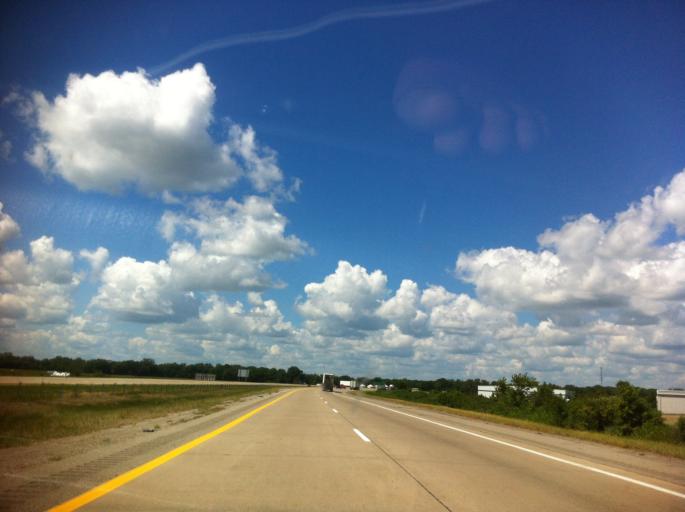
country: US
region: Michigan
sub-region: Monroe County
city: Dundee
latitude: 41.9699
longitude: -83.6756
